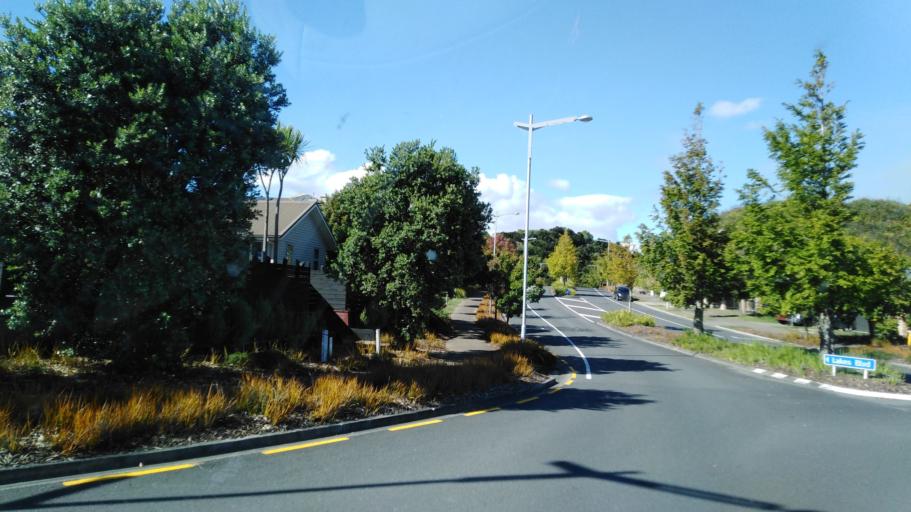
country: NZ
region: Bay of Plenty
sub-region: Tauranga City
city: Tauranga
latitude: -37.7414
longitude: 176.1103
